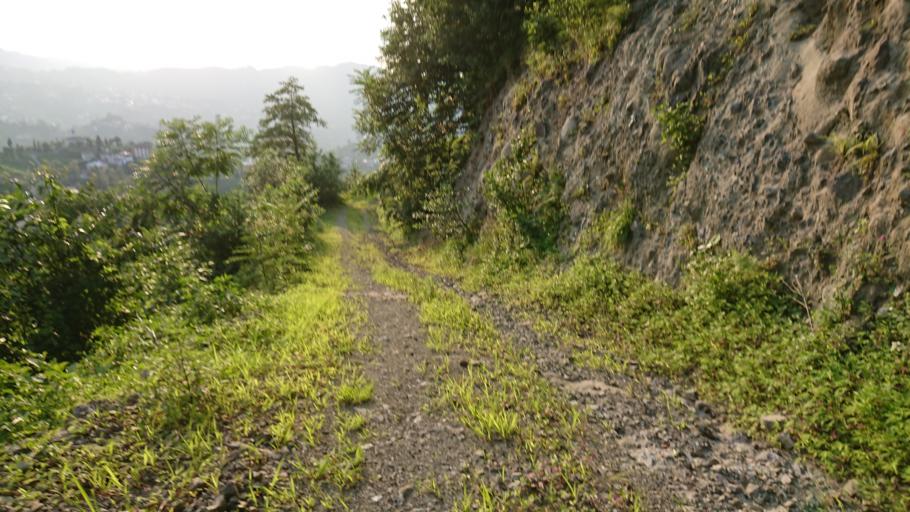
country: TR
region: Rize
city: Rize
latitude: 40.9912
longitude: 40.5015
